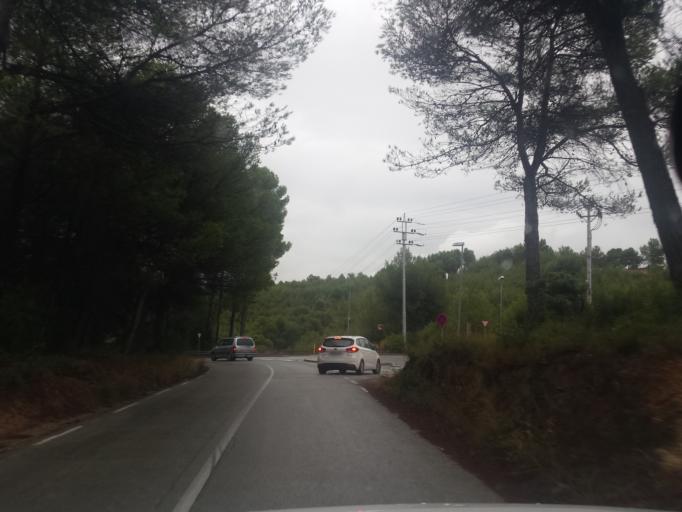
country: ES
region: Catalonia
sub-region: Provincia de Barcelona
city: Sant Andreu de la Barca
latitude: 41.4409
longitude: 1.9522
